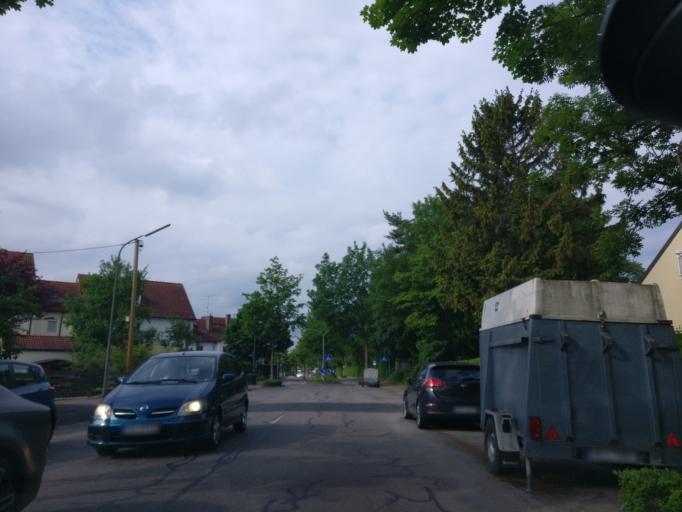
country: DE
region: Bavaria
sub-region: Upper Bavaria
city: Karlsfeld
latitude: 48.2343
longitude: 11.4716
